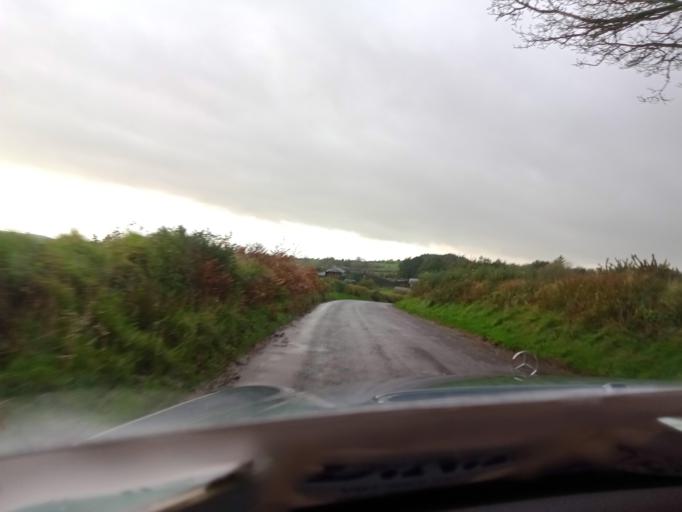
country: IE
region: Leinster
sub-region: Kilkenny
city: Mooncoin
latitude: 52.2619
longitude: -7.1998
